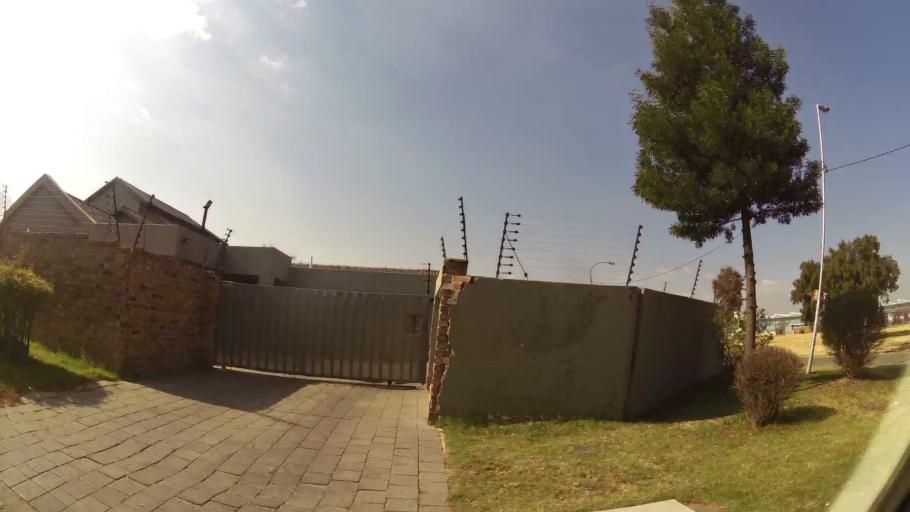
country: ZA
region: Gauteng
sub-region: Ekurhuleni Metropolitan Municipality
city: Boksburg
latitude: -26.1908
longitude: 28.2138
